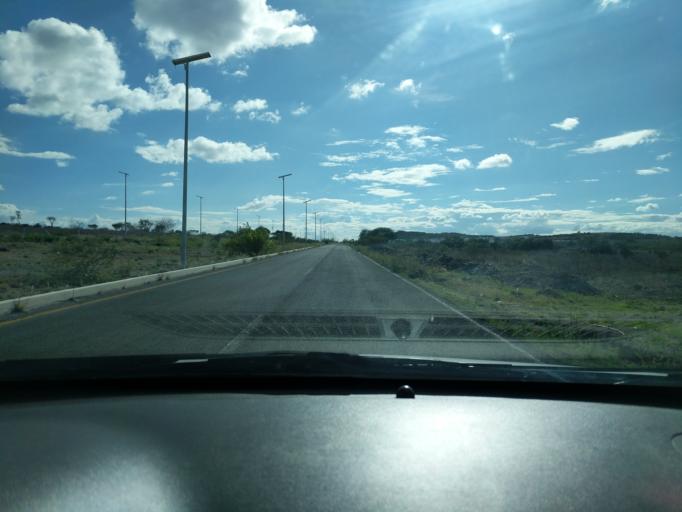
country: MX
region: Queretaro
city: La Canada
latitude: 20.5969
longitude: -100.2979
